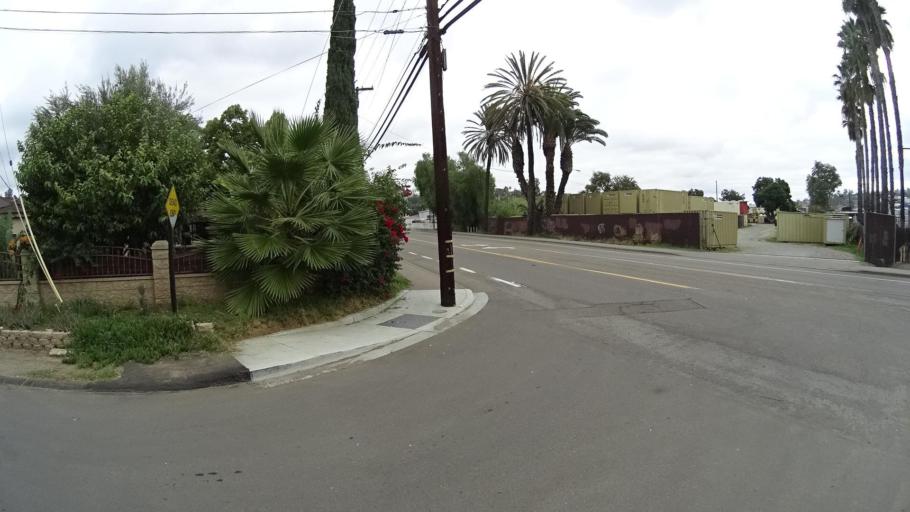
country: US
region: California
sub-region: San Diego County
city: Spring Valley
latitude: 32.7434
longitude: -117.0043
